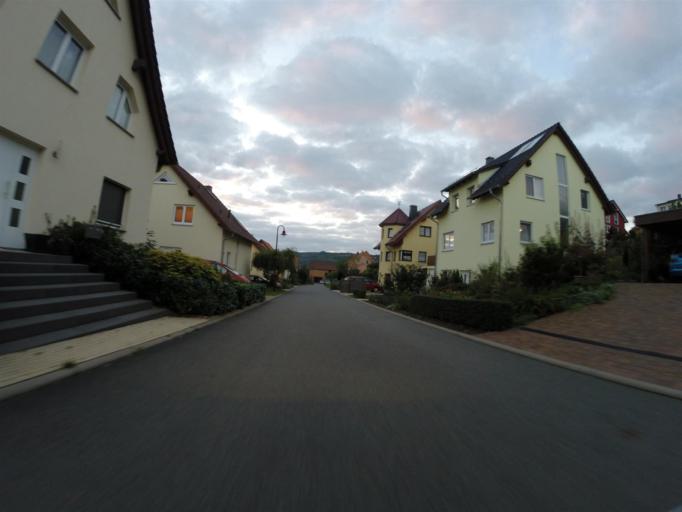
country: DE
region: Thuringia
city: Golmsdorf
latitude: 50.9522
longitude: 11.6384
